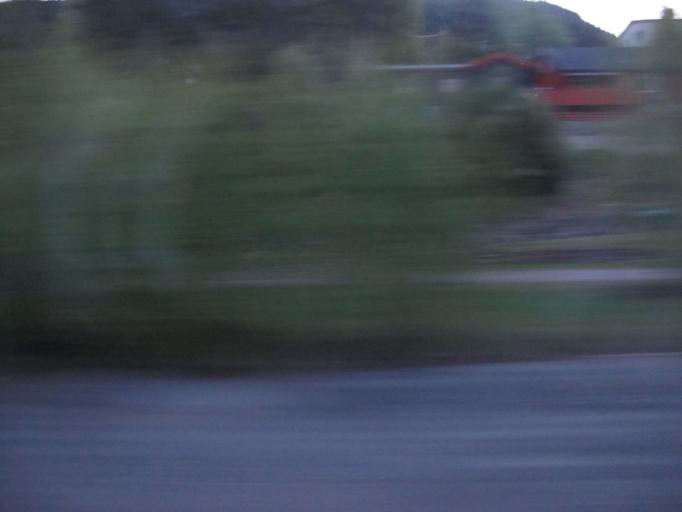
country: NO
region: Oppland
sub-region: Sor-Fron
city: Hundorp
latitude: 61.5752
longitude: 9.8567
